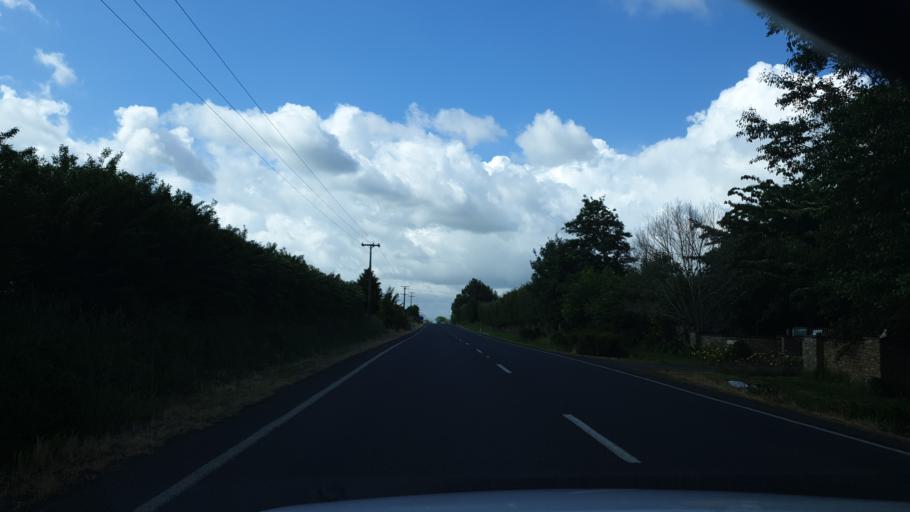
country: NZ
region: Waikato
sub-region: Hauraki District
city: Paeroa
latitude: -37.5105
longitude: 175.4961
